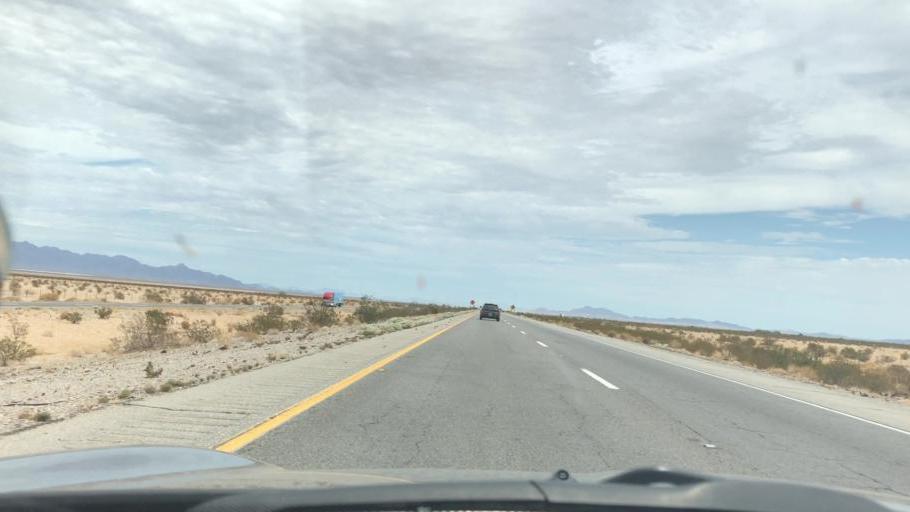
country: US
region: California
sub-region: Riverside County
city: Mesa Verde
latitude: 33.6390
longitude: -115.0951
